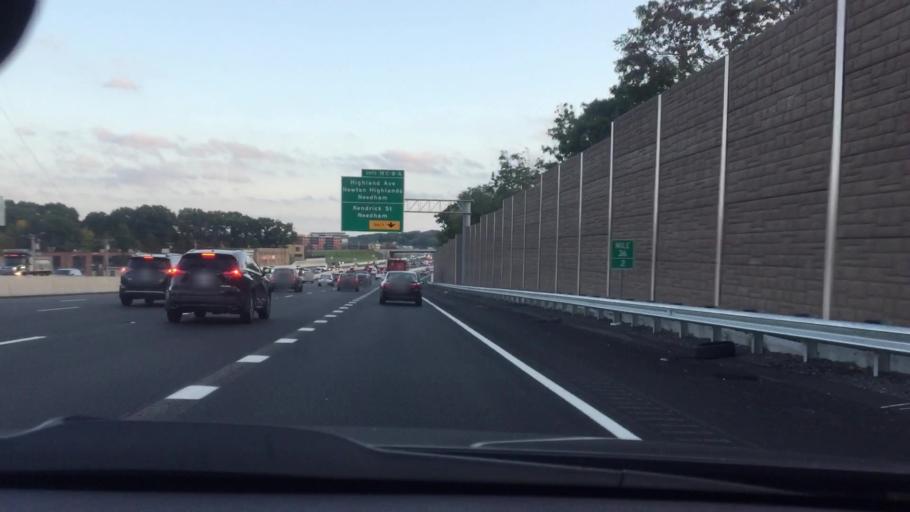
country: US
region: Massachusetts
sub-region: Norfolk County
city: Needham
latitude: 42.3090
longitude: -71.2287
